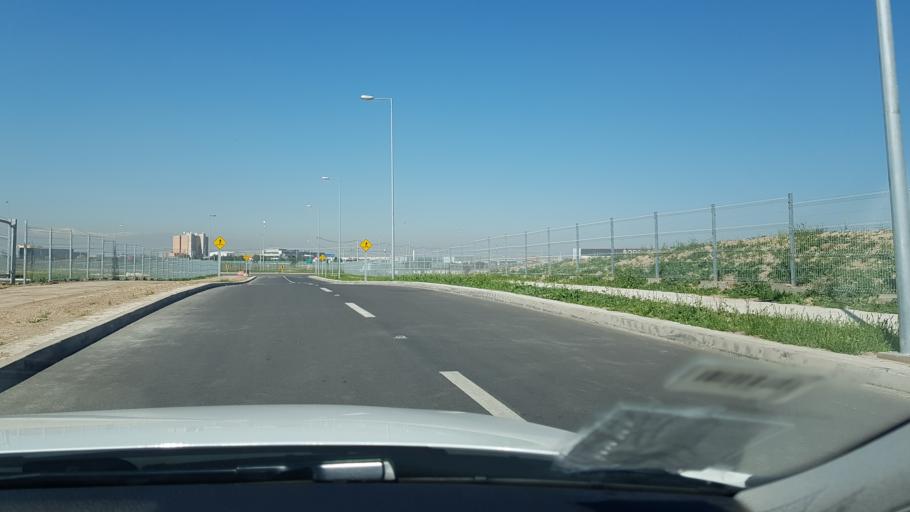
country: CL
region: Santiago Metropolitan
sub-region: Provincia de Santiago
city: Lo Prado
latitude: -33.4221
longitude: -70.7901
